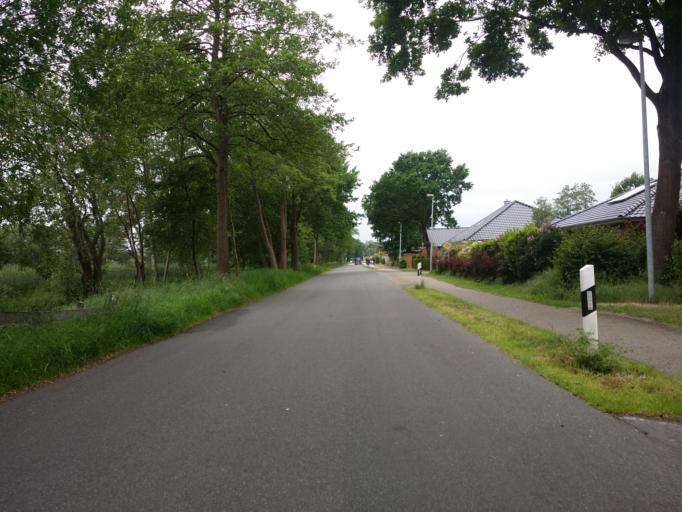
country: DE
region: Lower Saxony
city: Hatten
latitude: 53.1142
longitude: 8.3422
